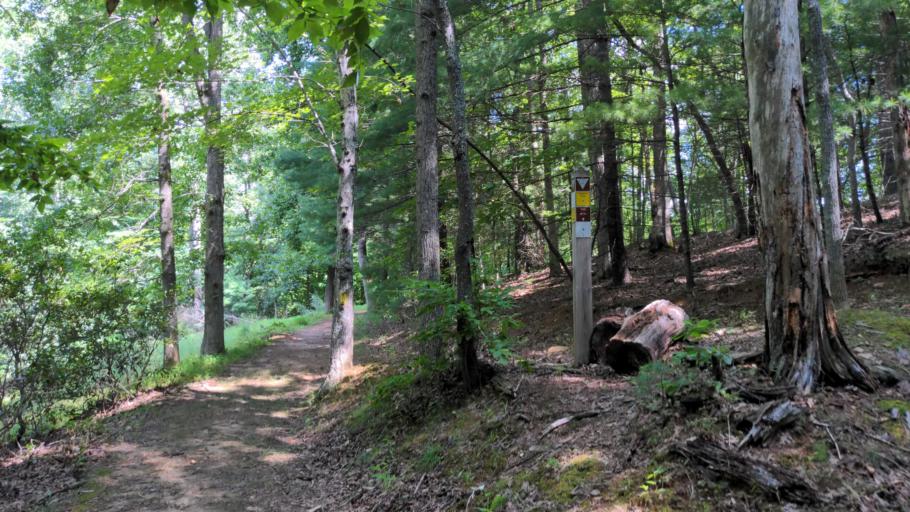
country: US
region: Virginia
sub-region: Henry County
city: Bassett
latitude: 36.7975
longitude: -80.1058
